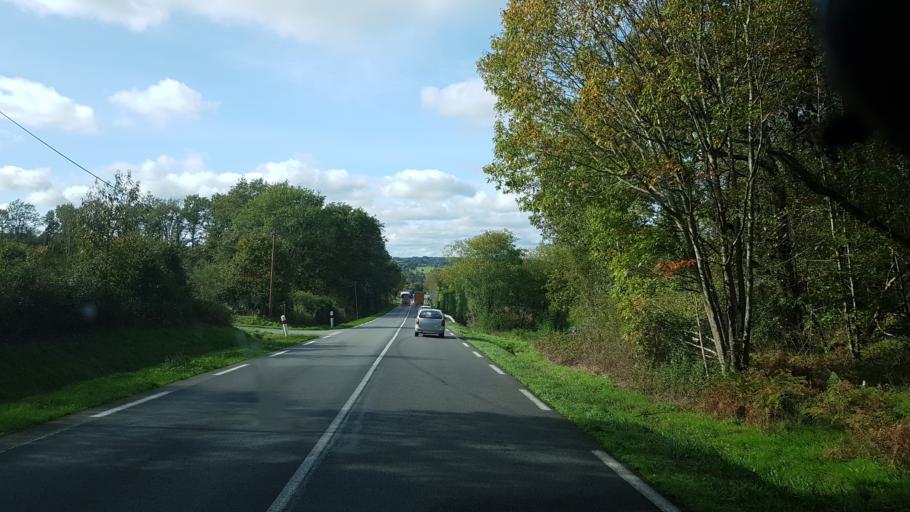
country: FR
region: Poitou-Charentes
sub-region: Departement de la Charente
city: Confolens
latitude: 46.0620
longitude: 0.6986
